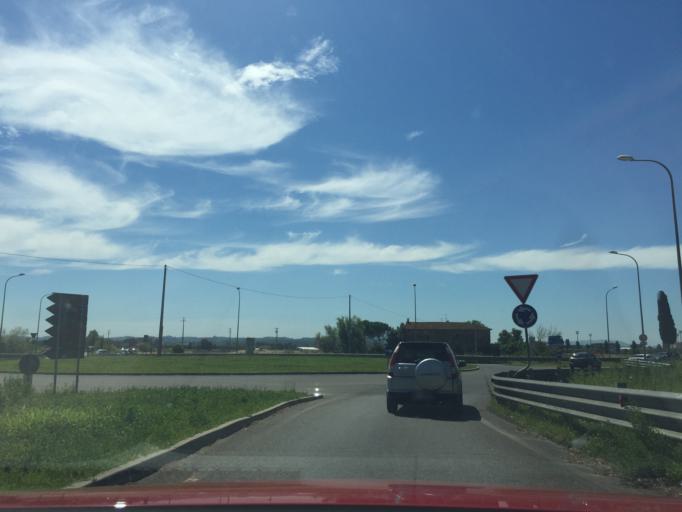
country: IT
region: Tuscany
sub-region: Province of Pisa
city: Pontedera
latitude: 43.6759
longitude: 10.6434
